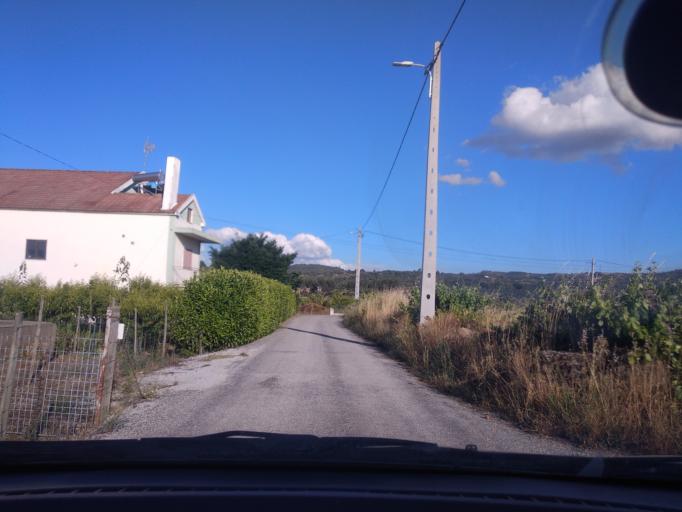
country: PT
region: Castelo Branco
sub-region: Covilha
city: Teixoso
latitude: 40.2532
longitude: -7.4046
